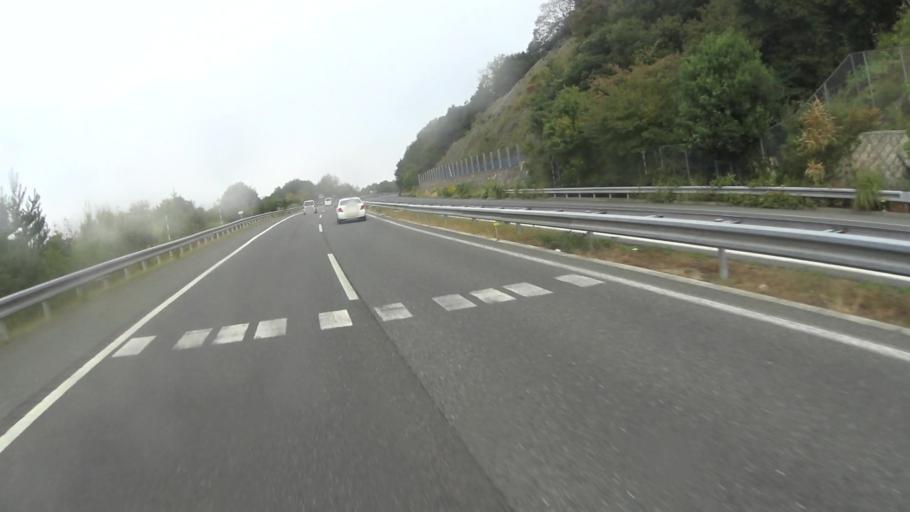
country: JP
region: Kyoto
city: Kameoka
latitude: 35.1026
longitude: 135.4902
